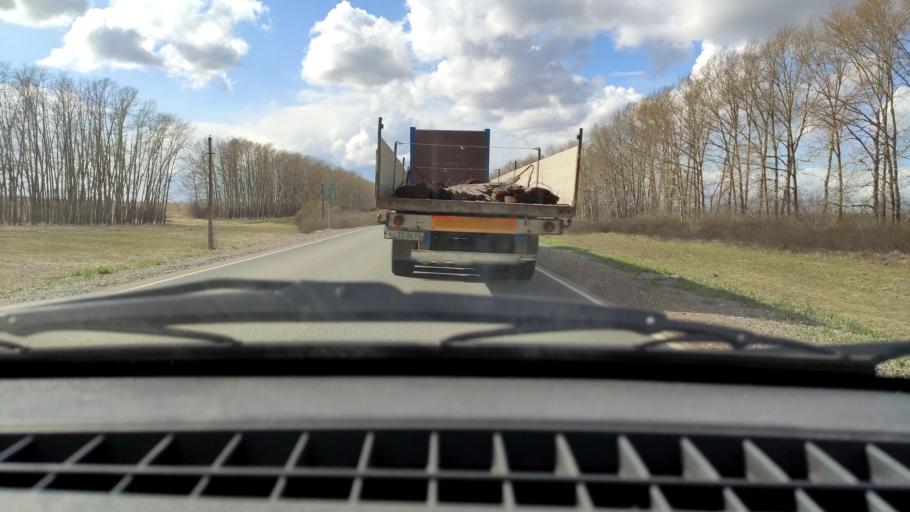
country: RU
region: Bashkortostan
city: Alekseyevka
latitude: 55.0583
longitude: 55.1122
